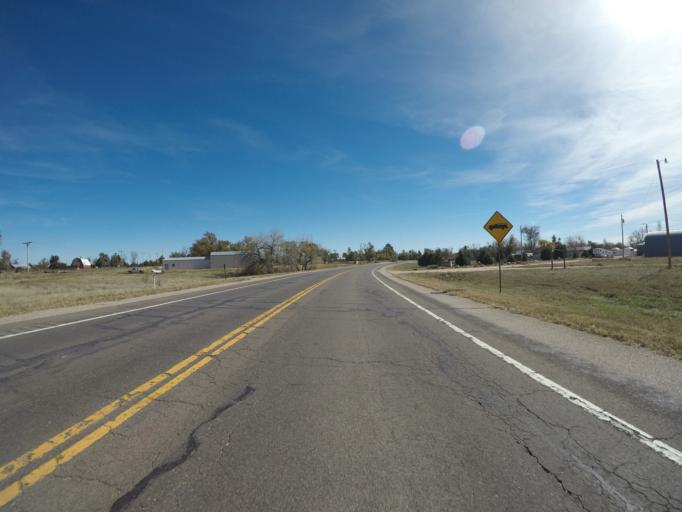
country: US
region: Colorado
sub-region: Yuma County
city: Yuma
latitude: 39.6696
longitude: -102.8538
